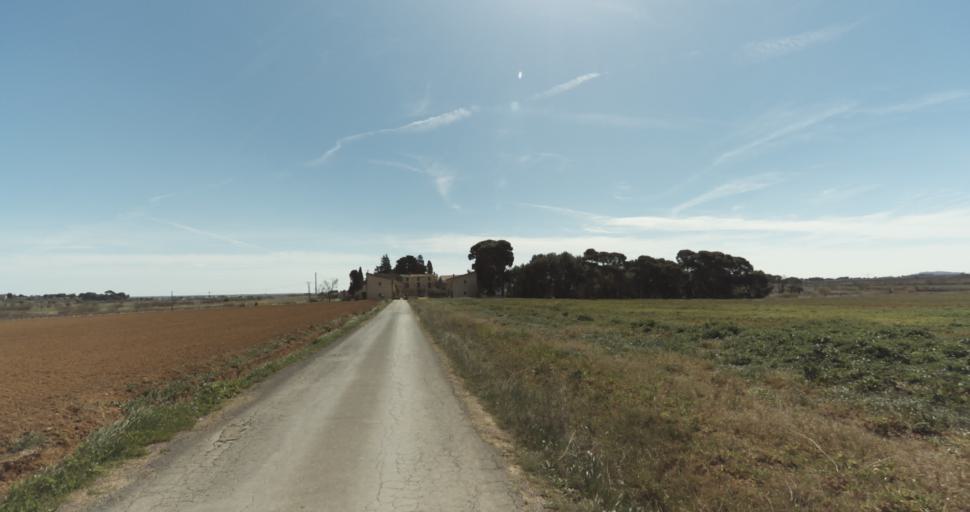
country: FR
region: Languedoc-Roussillon
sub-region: Departement de l'Herault
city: Marseillan
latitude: 43.3873
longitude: 3.5432
